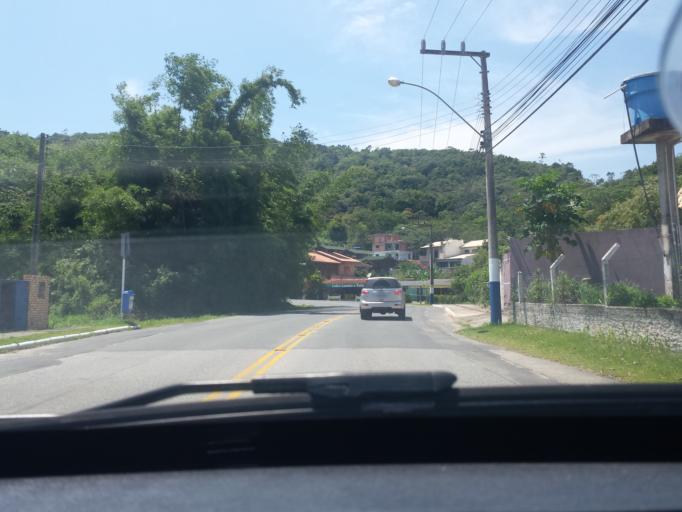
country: BR
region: Santa Catarina
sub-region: Balneario Camboriu
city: Balneario Camboriu
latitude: -27.0121
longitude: -48.5810
